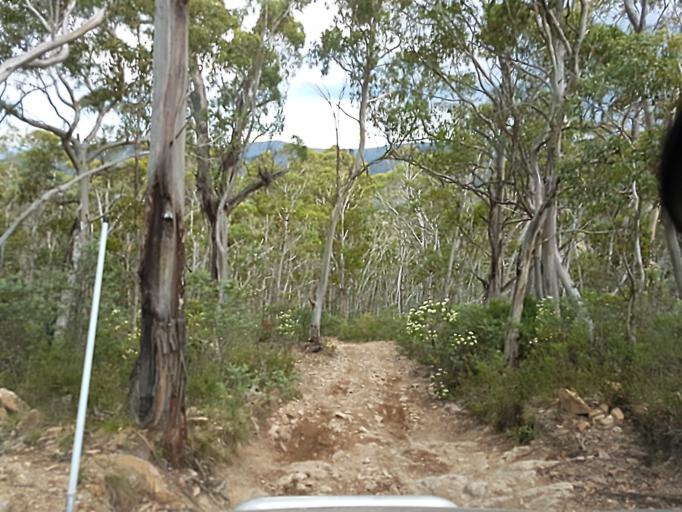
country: AU
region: New South Wales
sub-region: Snowy River
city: Jindabyne
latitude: -36.8798
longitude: 148.2028
